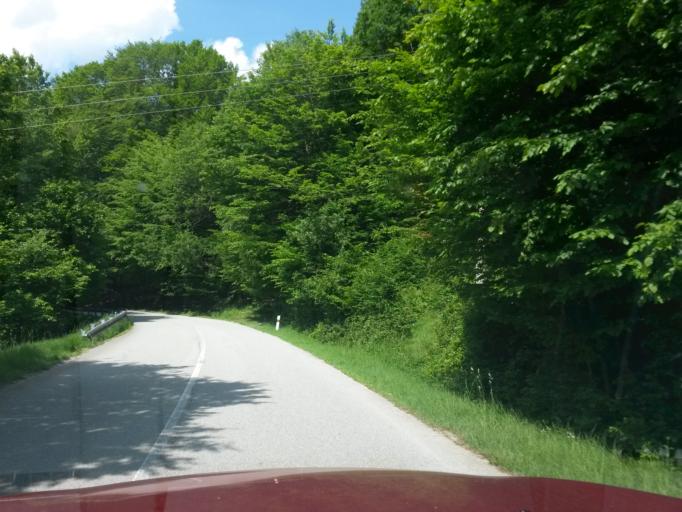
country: SK
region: Kosicky
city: Medzev
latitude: 48.7247
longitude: 20.7826
